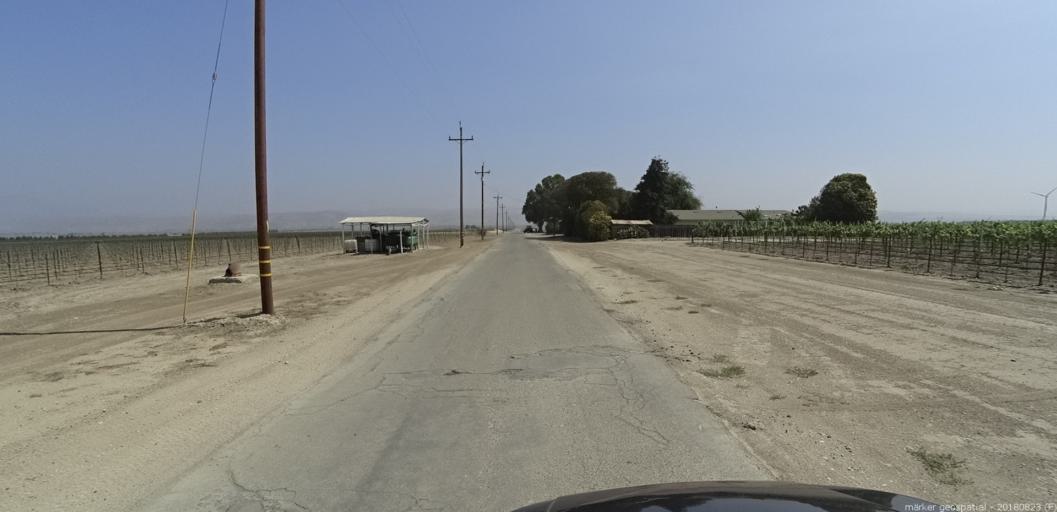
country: US
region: California
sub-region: Monterey County
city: Greenfield
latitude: 36.2791
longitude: -121.2113
